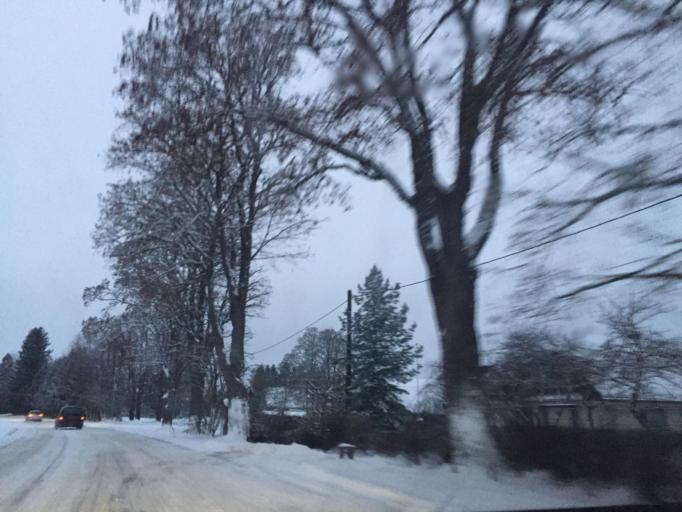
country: LV
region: Raunas
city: Rauna
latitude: 57.4215
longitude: 25.5759
